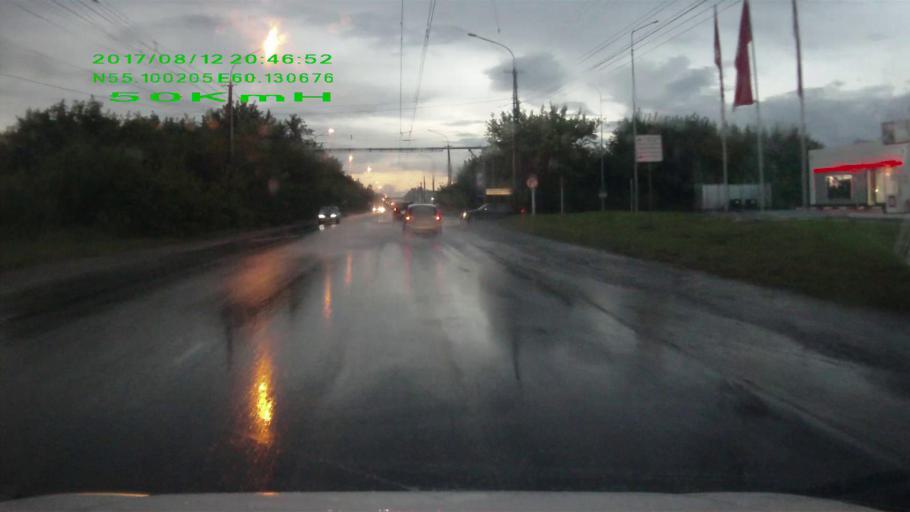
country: RU
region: Chelyabinsk
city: Turgoyak
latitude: 55.1004
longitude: 60.1307
